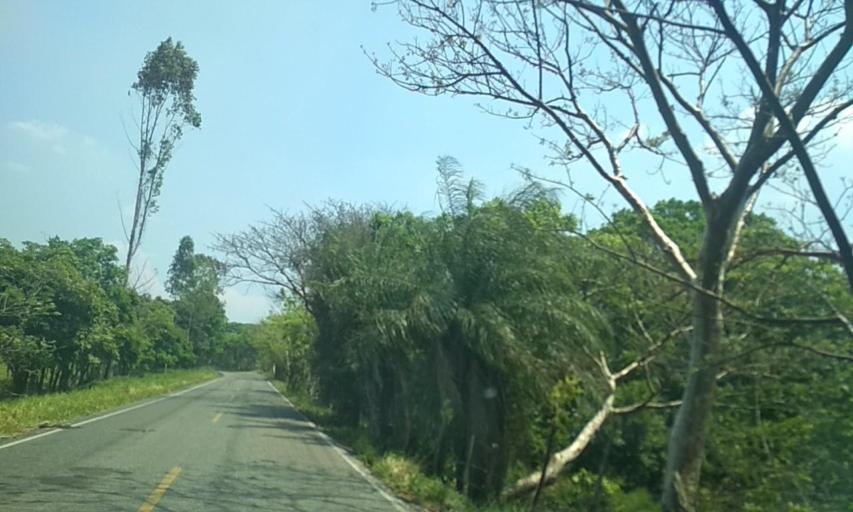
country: MX
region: Tabasco
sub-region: Huimanguillo
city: C-41 (Licenciado Carlos A. Madrazo)
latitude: 17.8420
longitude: -93.5221
